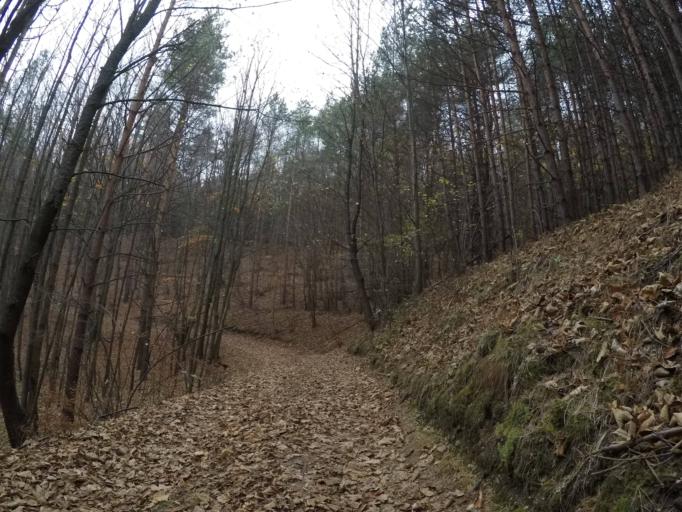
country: SK
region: Presovsky
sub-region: Okres Presov
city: Presov
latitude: 48.8993
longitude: 21.1684
